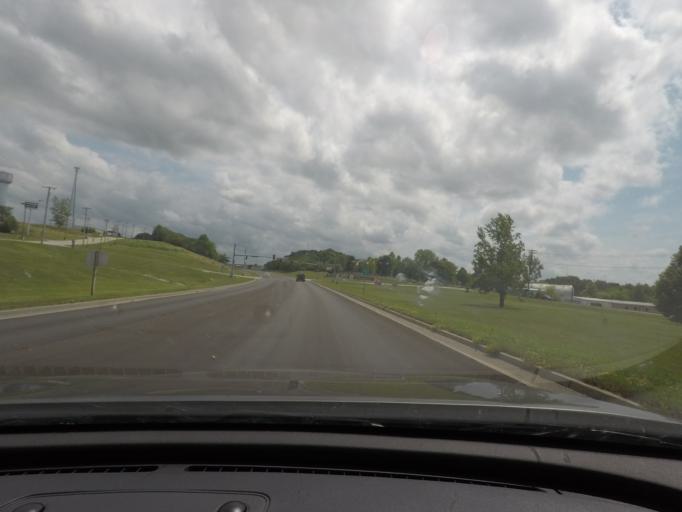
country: US
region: Missouri
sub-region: Carroll County
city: Carrollton
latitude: 39.3675
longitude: -93.4849
